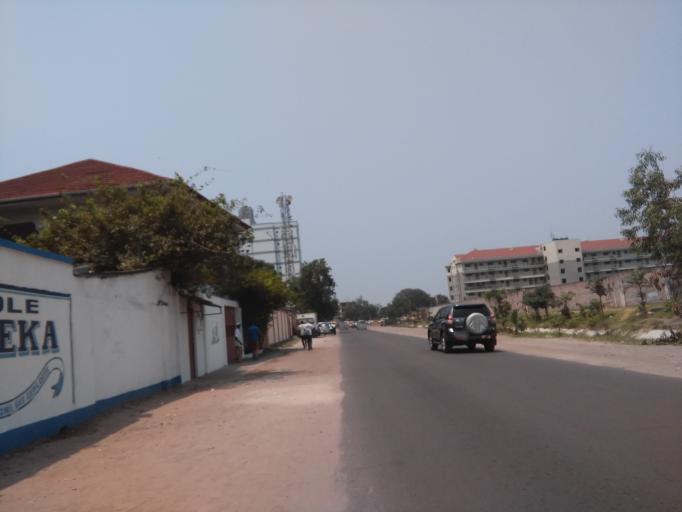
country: CD
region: Kinshasa
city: Kinshasa
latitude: -4.3175
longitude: 15.2901
